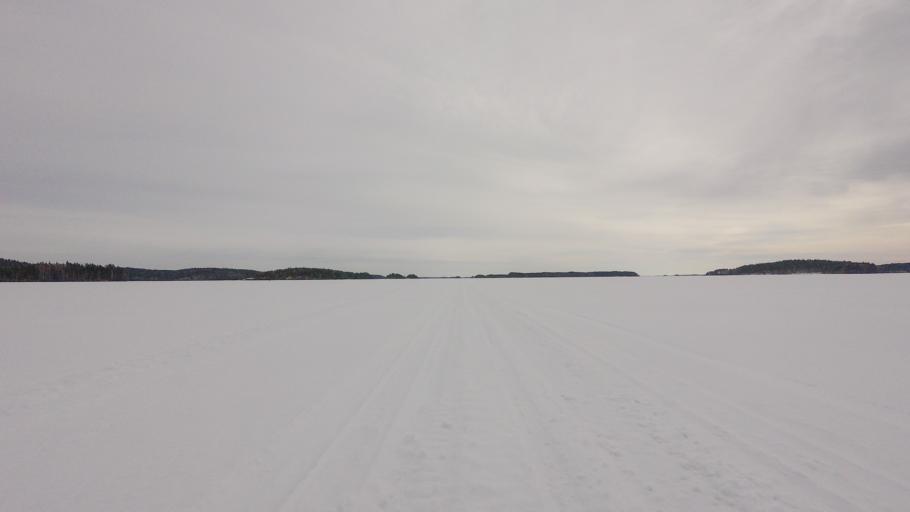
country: FI
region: Southern Savonia
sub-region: Savonlinna
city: Rantasalmi
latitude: 62.0996
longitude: 28.4714
